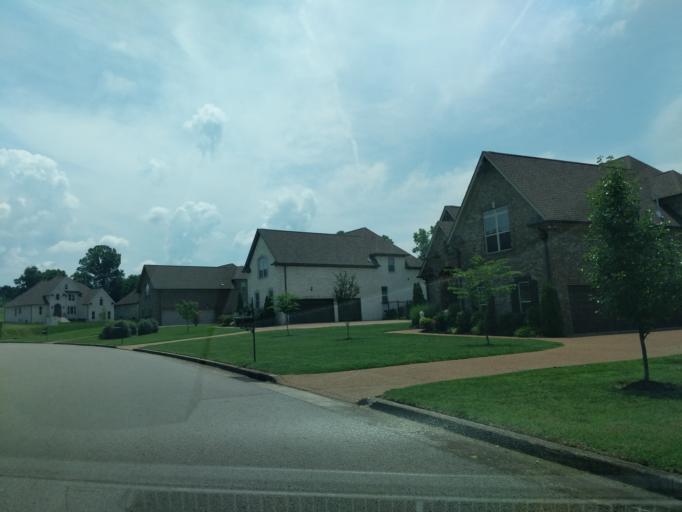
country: US
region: Tennessee
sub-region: Davidson County
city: Lakewood
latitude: 36.2290
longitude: -86.6287
